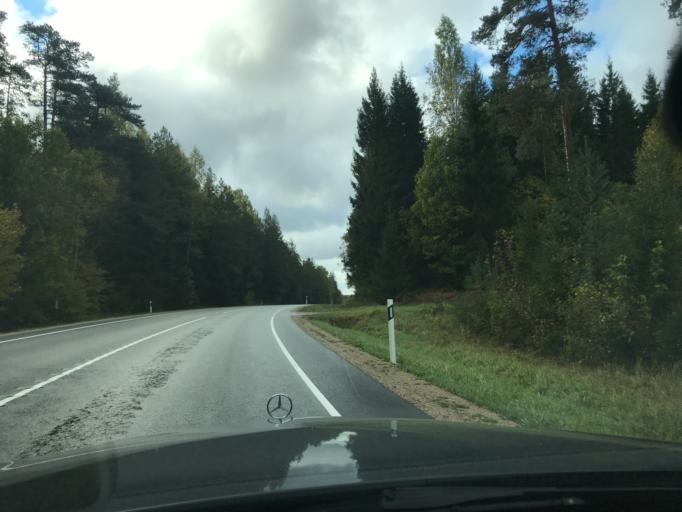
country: EE
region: Viljandimaa
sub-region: Karksi vald
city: Karksi-Nuia
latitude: 58.0431
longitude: 25.6466
